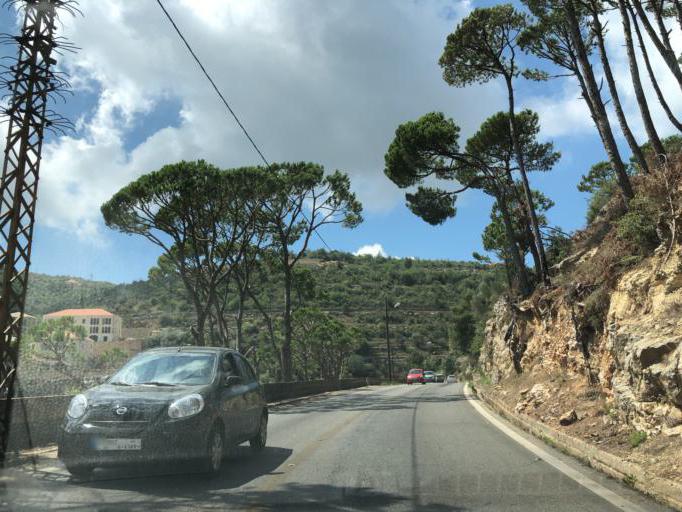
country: LB
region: Mont-Liban
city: Beit ed Dine
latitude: 33.7009
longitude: 35.5800
